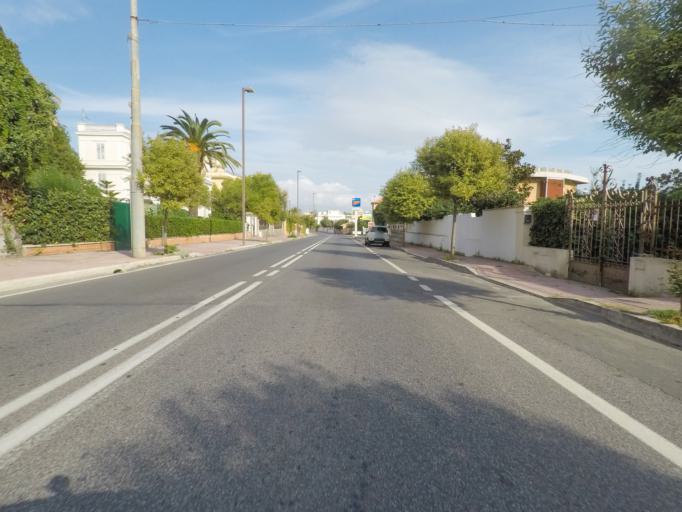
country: IT
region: Latium
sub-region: Citta metropolitana di Roma Capitale
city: Santa Marinella
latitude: 42.0336
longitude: 11.8548
